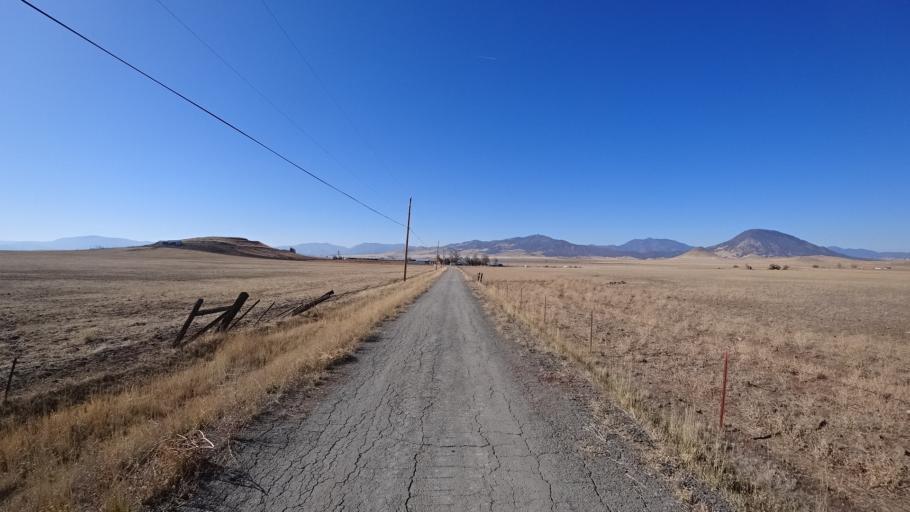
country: US
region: California
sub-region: Siskiyou County
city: Montague
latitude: 41.7939
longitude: -122.4257
